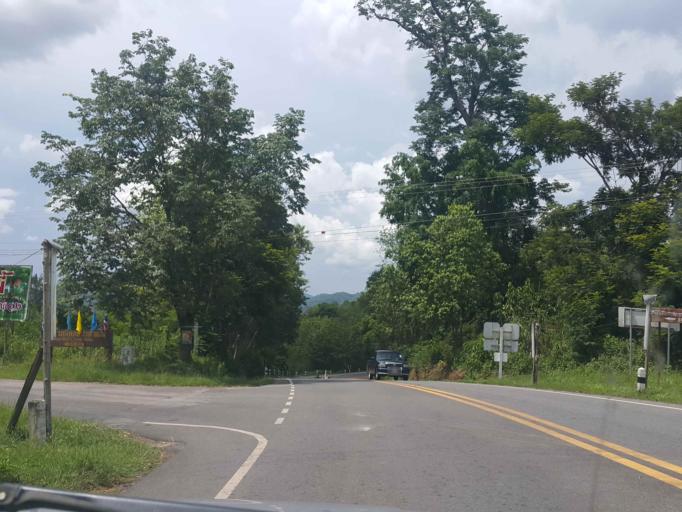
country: TH
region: Nan
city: Ban Luang
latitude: 18.8589
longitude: 100.4551
